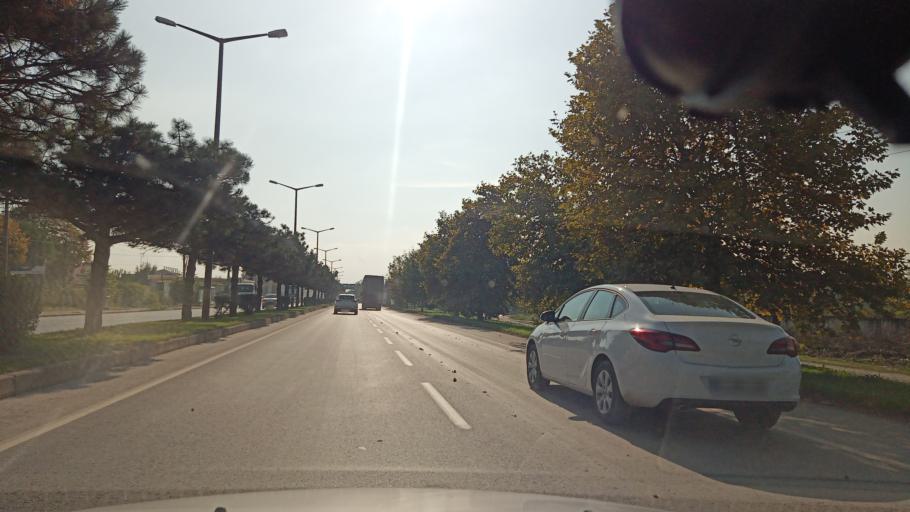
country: TR
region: Sakarya
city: Adapazari
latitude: 40.8058
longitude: 30.4057
